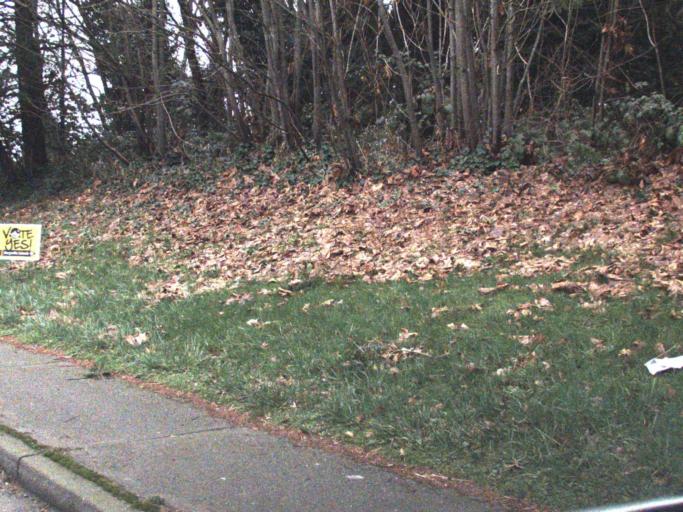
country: US
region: Washington
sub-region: Snohomish County
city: Marysville
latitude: 48.0521
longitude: -122.1632
